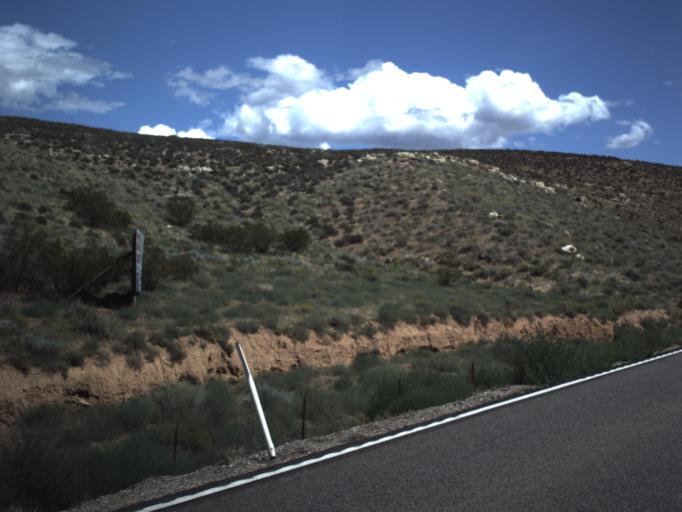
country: US
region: Utah
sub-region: Washington County
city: Hurricane
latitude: 37.1738
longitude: -113.2685
